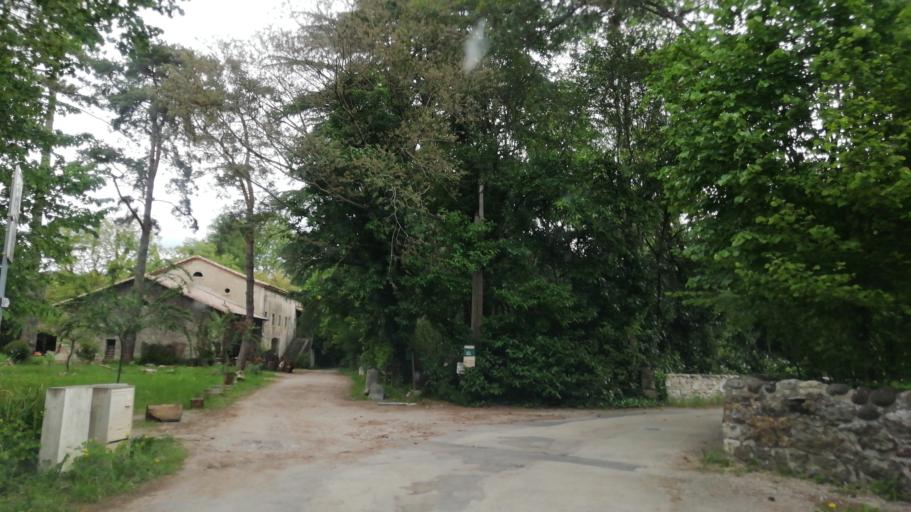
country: FR
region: Languedoc-Roussillon
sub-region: Departement de l'Herault
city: Cazilhac
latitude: 43.9232
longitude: 3.7107
